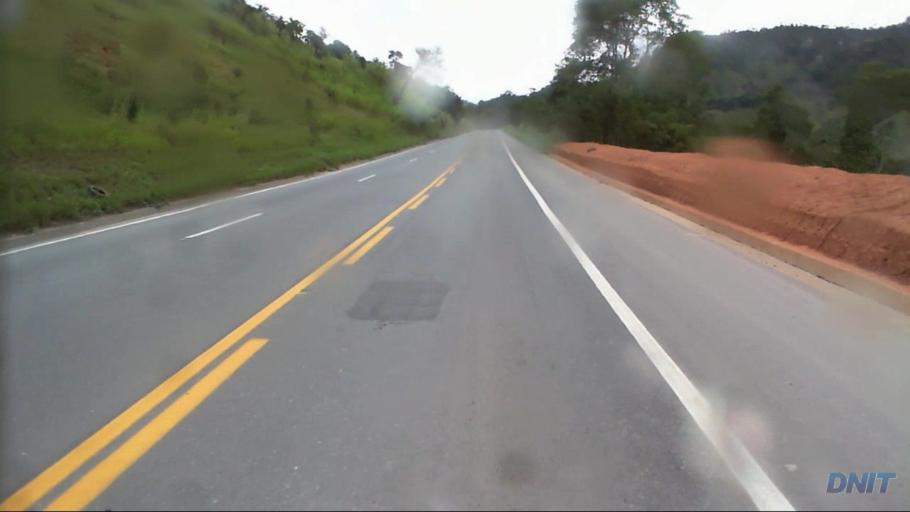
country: BR
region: Minas Gerais
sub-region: Nova Era
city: Nova Era
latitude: -19.7048
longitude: -42.9984
